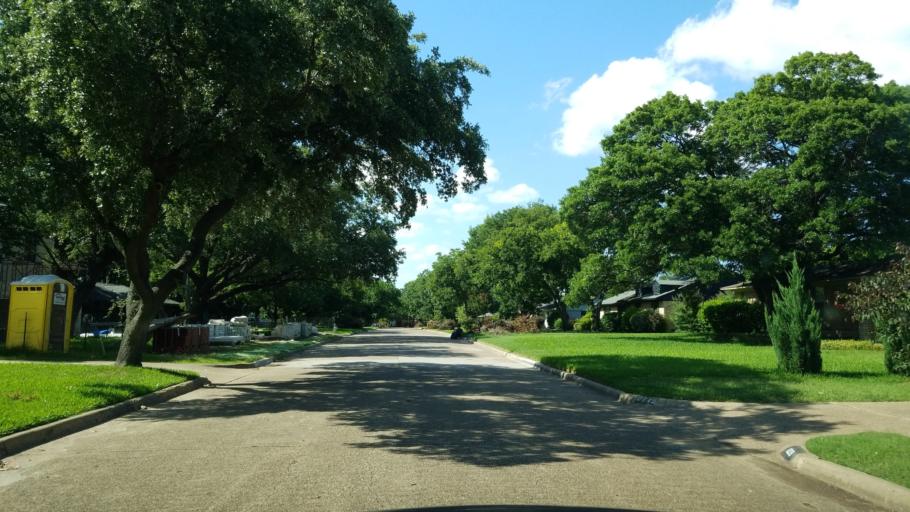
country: US
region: Texas
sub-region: Dallas County
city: University Park
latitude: 32.8853
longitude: -96.8487
